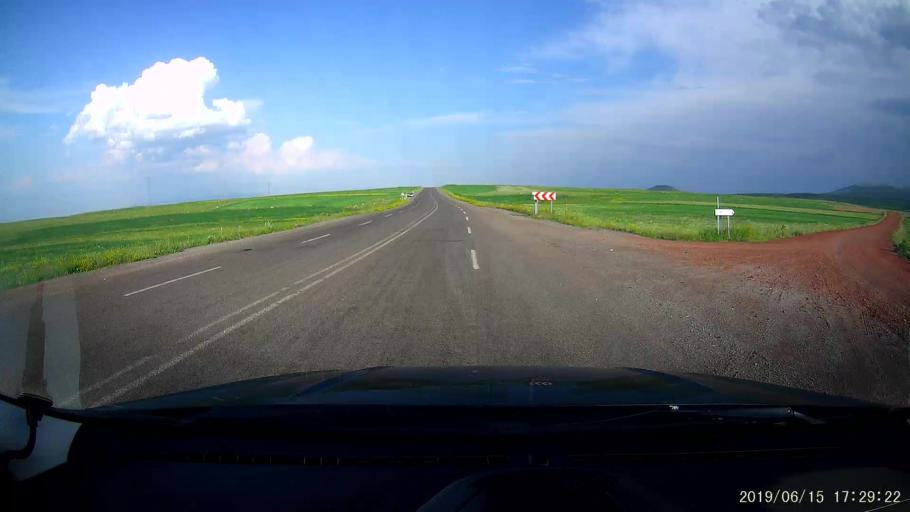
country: TR
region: Kars
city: Basgedikler
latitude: 40.5900
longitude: 43.4516
